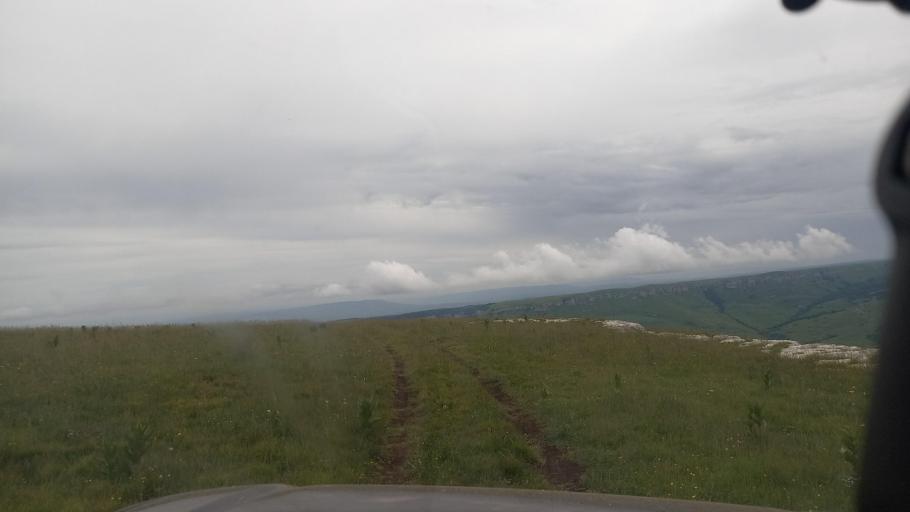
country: RU
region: Karachayevo-Cherkesiya
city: Pregradnaya
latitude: 43.9735
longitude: 41.2923
